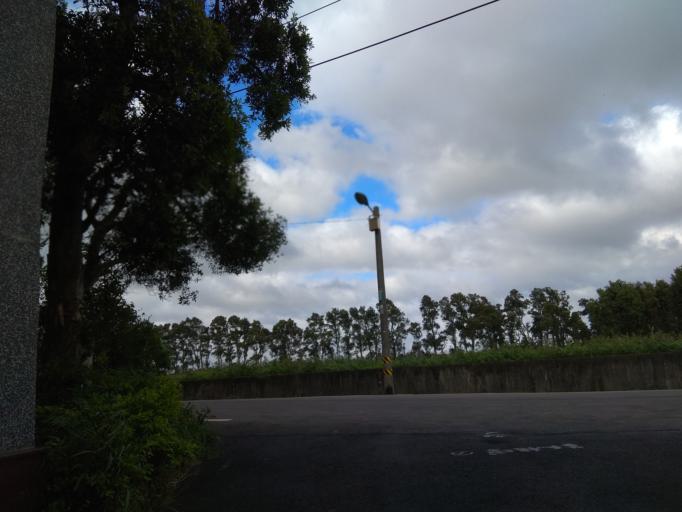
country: TW
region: Taiwan
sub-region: Hsinchu
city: Zhubei
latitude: 24.9734
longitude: 121.0851
